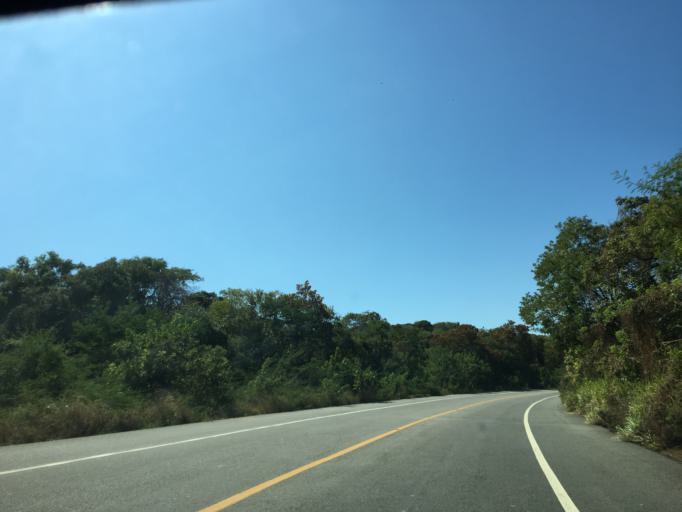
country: MX
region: Oaxaca
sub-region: Santa Maria Huatulco
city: Sector H Tres
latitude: 15.7754
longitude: -96.2218
